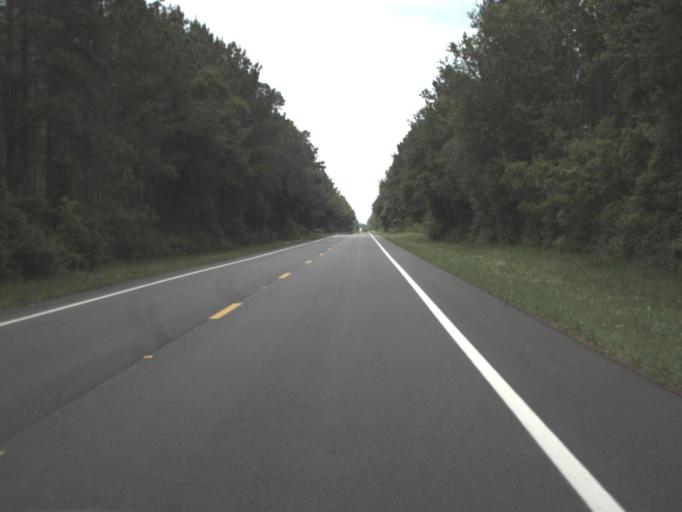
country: US
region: Florida
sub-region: Hamilton County
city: Jasper
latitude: 30.5676
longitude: -82.6801
